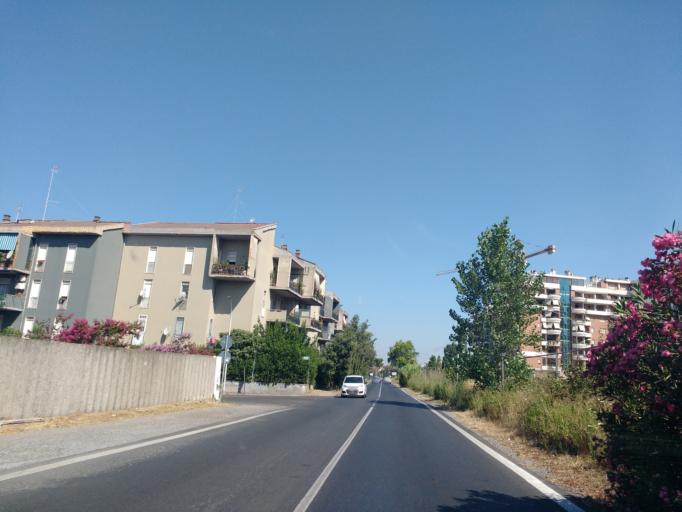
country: IT
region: Latium
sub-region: Citta metropolitana di Roma Capitale
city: Vitinia
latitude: 41.7709
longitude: 12.3733
